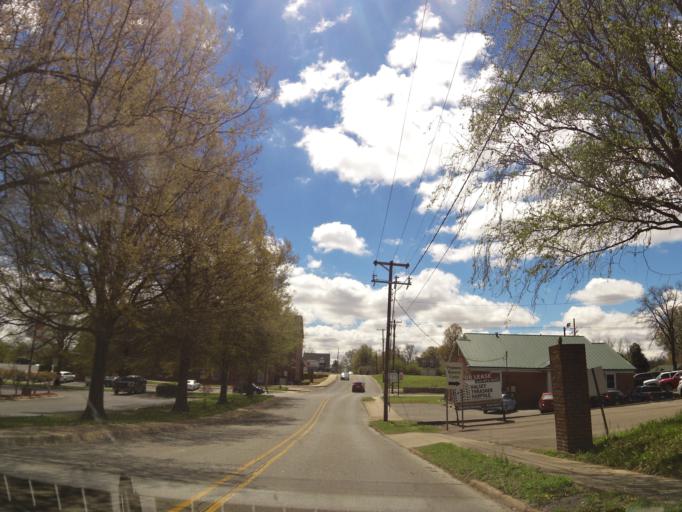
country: US
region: Arkansas
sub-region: Craighead County
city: Jonesboro
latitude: 35.8345
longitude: -90.7041
